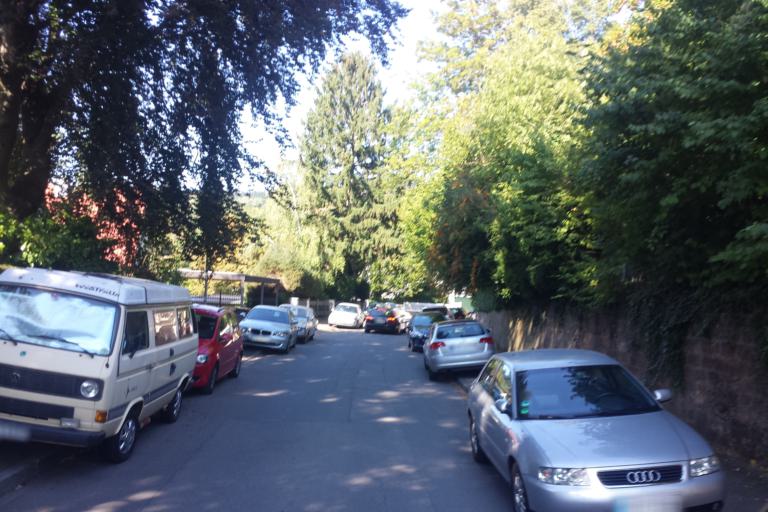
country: DE
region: Baden-Wuerttemberg
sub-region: Karlsruhe Region
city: Heidelberg
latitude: 49.4296
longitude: 8.6906
